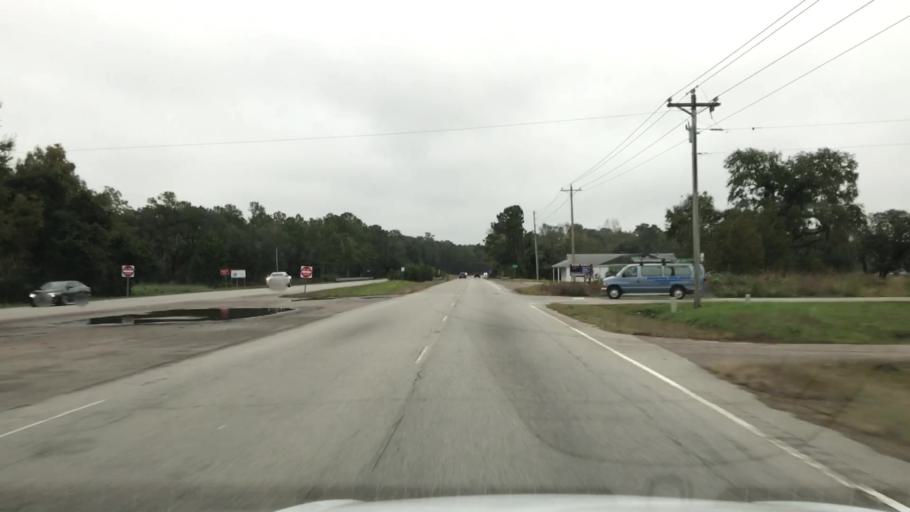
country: US
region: South Carolina
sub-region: Charleston County
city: Awendaw
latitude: 33.0289
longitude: -79.6265
